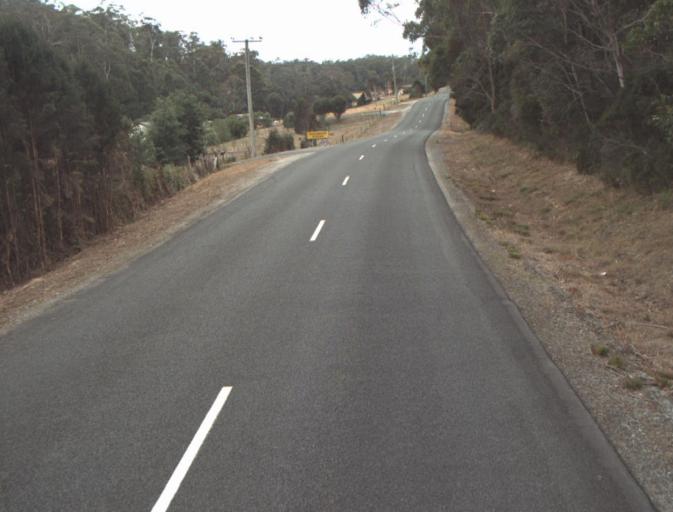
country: AU
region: Tasmania
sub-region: Launceston
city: Mayfield
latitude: -41.2388
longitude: 147.0181
